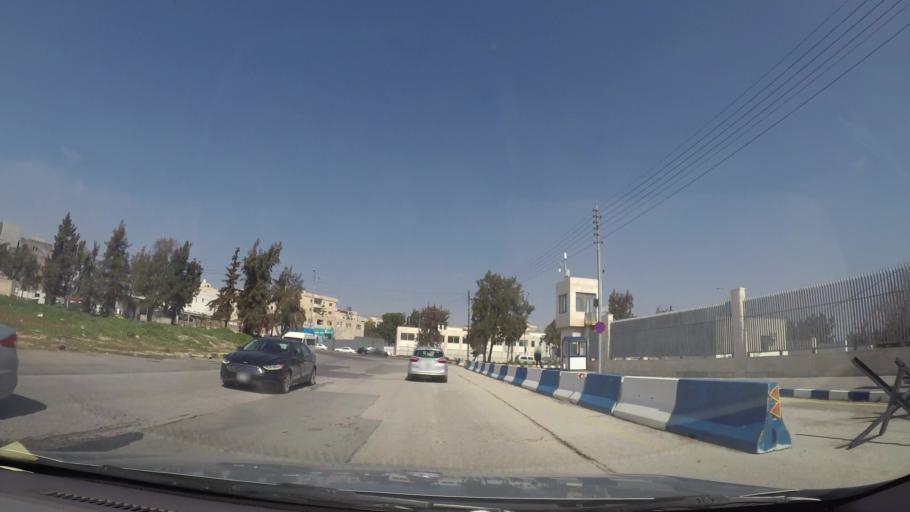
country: JO
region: Amman
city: Al Bunayyat ash Shamaliyah
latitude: 31.9015
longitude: 35.8742
